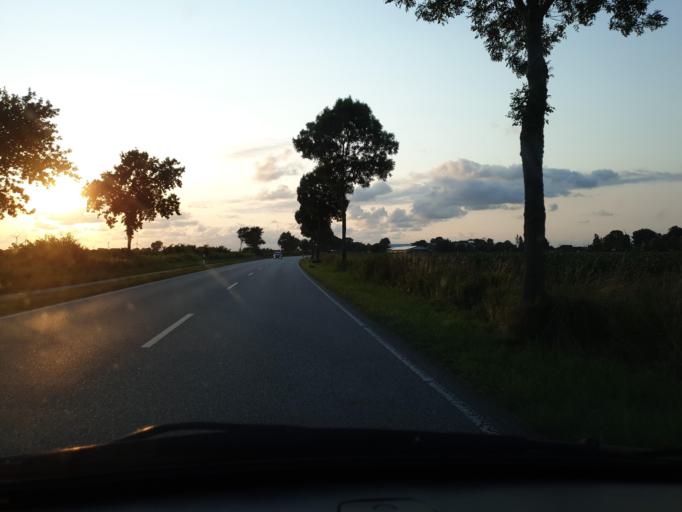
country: DE
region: Schleswig-Holstein
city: Schmedeswurth
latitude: 53.9114
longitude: 9.0548
